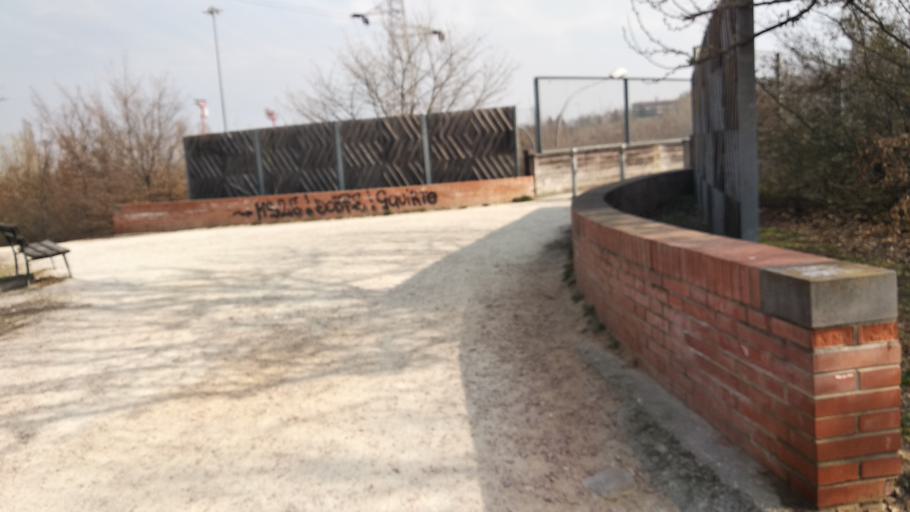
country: IT
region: Emilia-Romagna
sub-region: Provincia di Bologna
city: Ponticella
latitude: 44.4614
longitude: 11.3784
